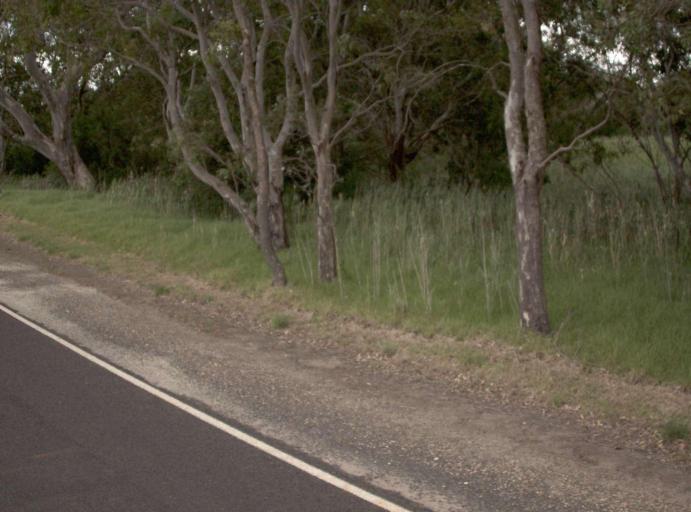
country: AU
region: Victoria
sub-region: Wellington
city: Sale
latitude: -38.0210
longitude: 147.1824
